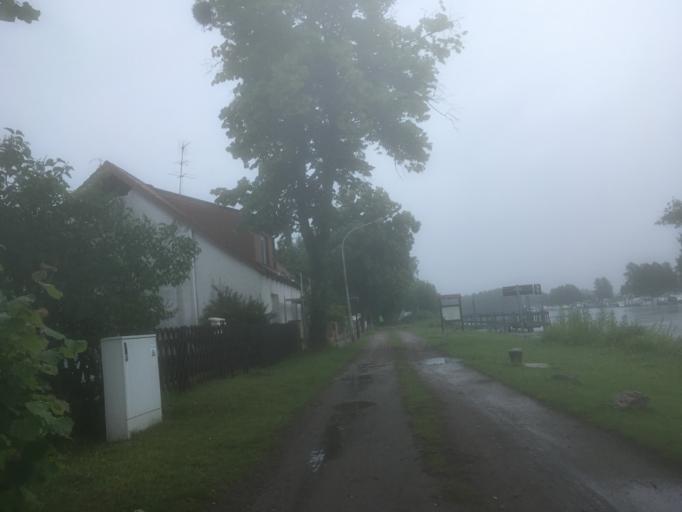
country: DE
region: Brandenburg
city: Zehdenick
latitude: 52.9839
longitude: 13.3307
